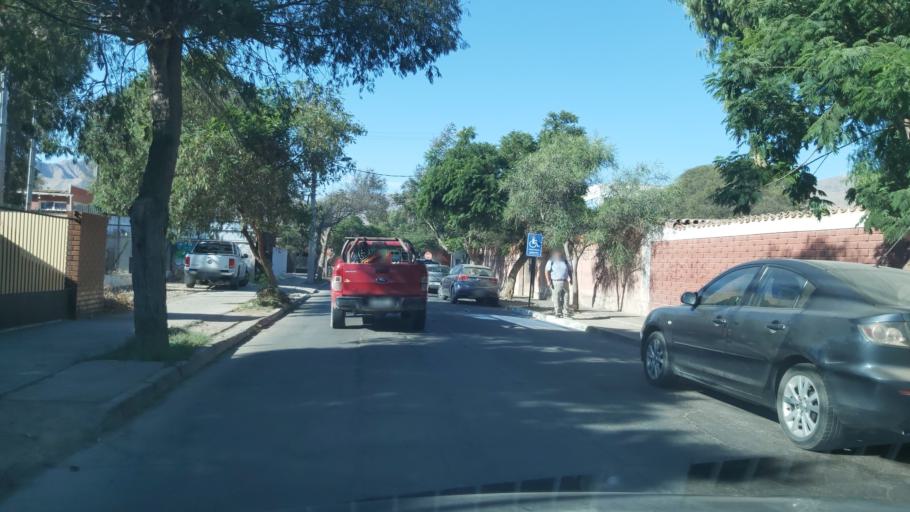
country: CL
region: Atacama
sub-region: Provincia de Copiapo
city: Copiapo
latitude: -27.3753
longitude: -70.3246
